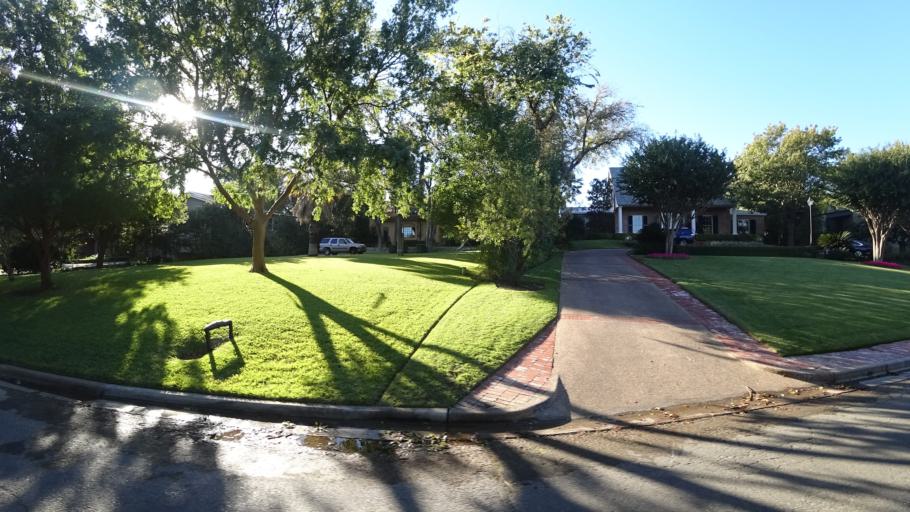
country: US
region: Texas
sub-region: Travis County
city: Austin
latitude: 30.2954
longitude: -97.7506
